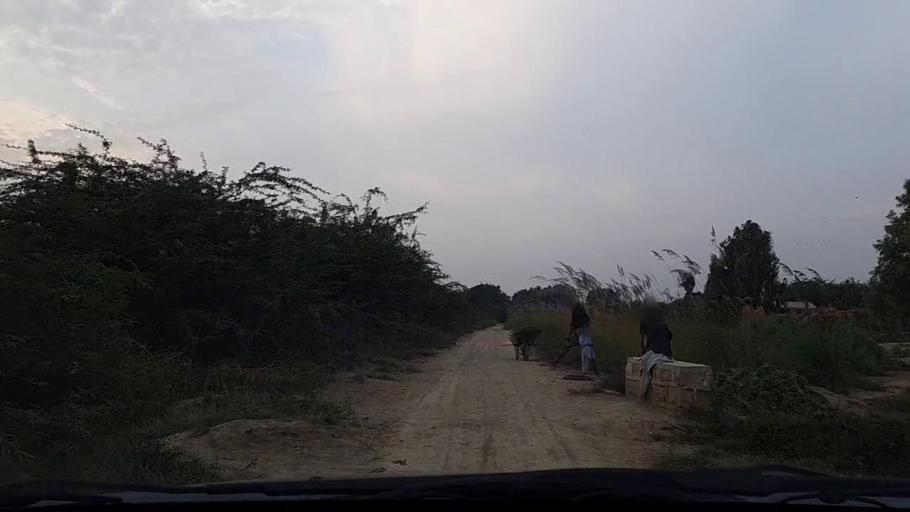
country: PK
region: Sindh
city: Thatta
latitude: 24.7708
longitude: 67.9228
